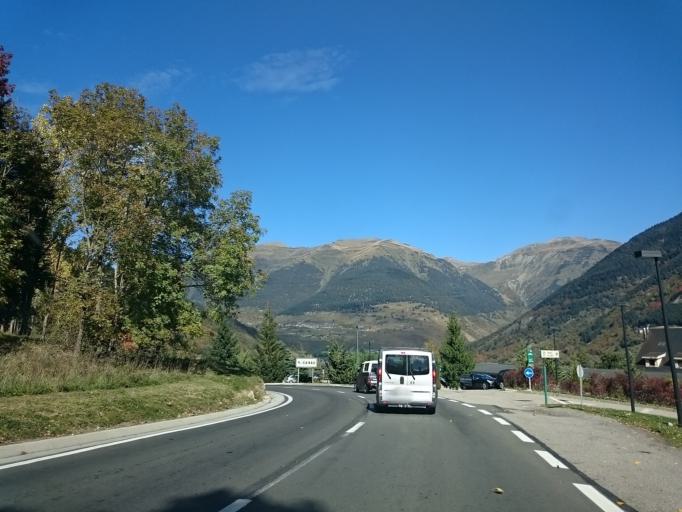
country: ES
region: Catalonia
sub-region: Provincia de Lleida
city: Vielha
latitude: 42.6988
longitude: 0.7890
